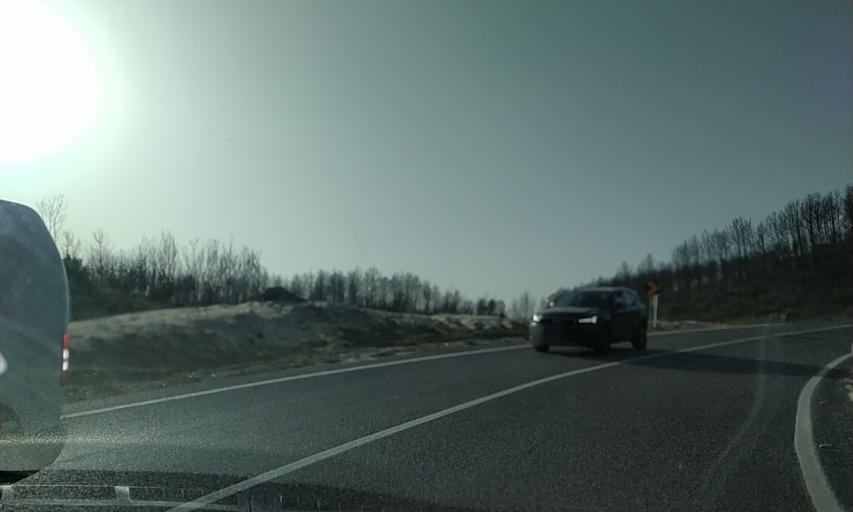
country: PT
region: Leiria
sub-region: Marinha Grande
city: Marinha Grande
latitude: 39.7458
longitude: -8.9873
